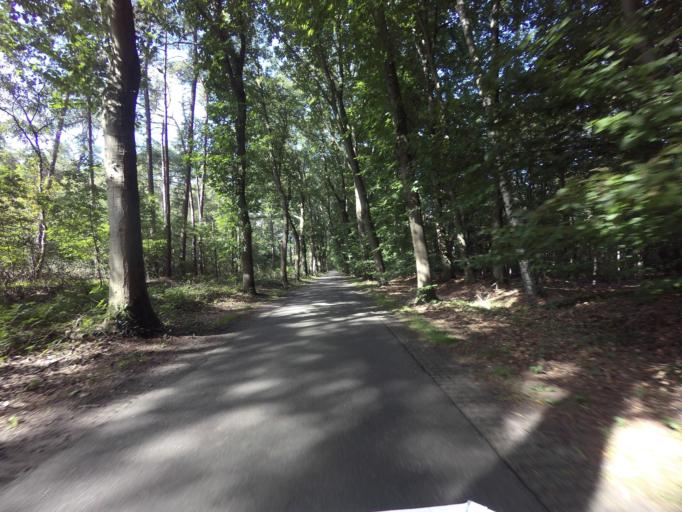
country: NL
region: Overijssel
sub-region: Gemeente Deventer
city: Schalkhaar
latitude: 52.3065
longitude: 6.2131
